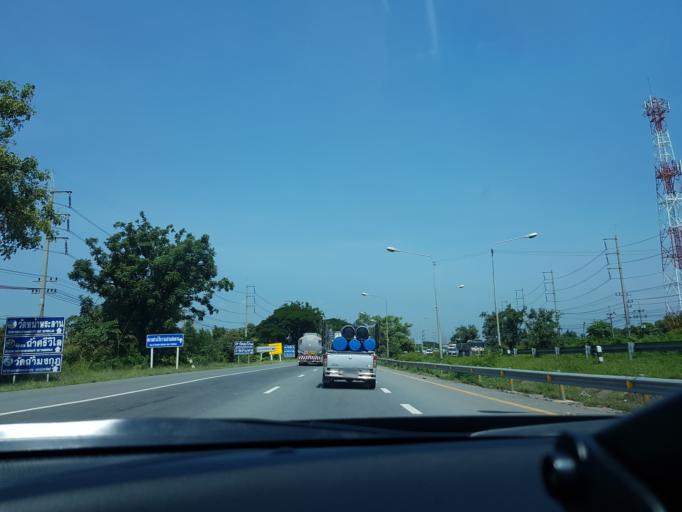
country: TH
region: Sara Buri
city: Saraburi
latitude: 14.5323
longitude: 100.8859
